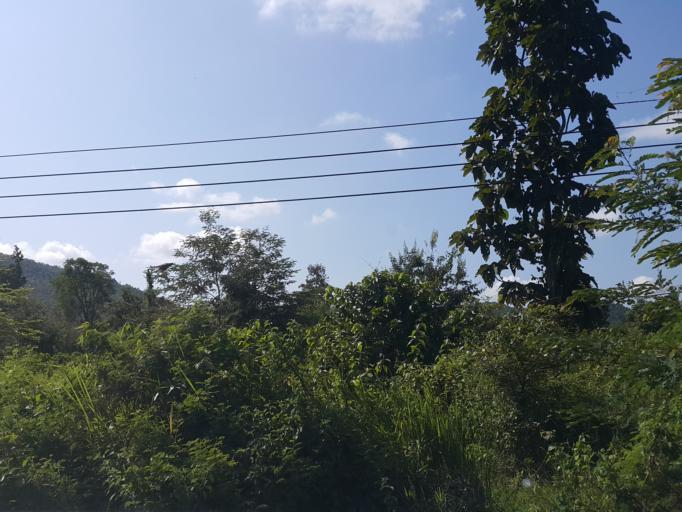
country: TH
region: Chiang Mai
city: Mae On
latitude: 18.8044
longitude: 99.1922
